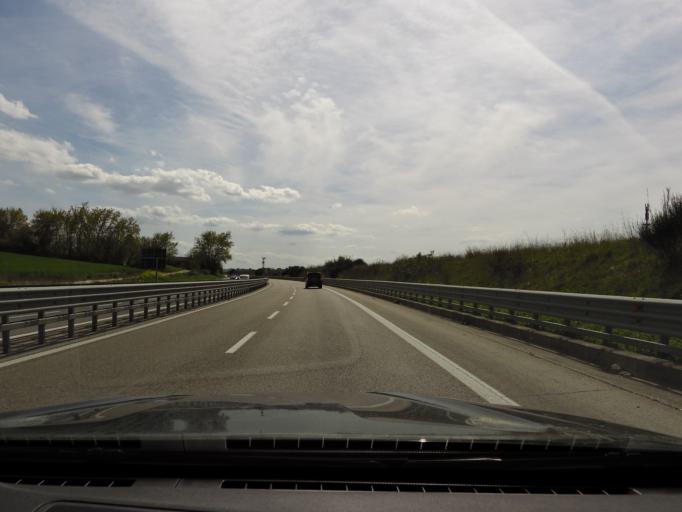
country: IT
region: The Marches
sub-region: Provincia di Ancona
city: San Biagio
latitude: 43.5424
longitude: 13.5142
